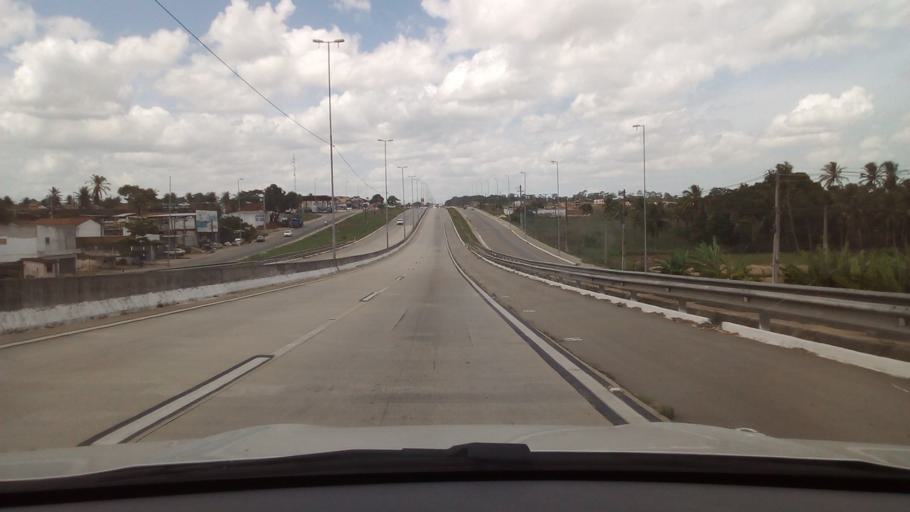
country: BR
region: Paraiba
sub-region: Mamanguape
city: Mamanguape
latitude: -6.8376
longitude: -35.1365
